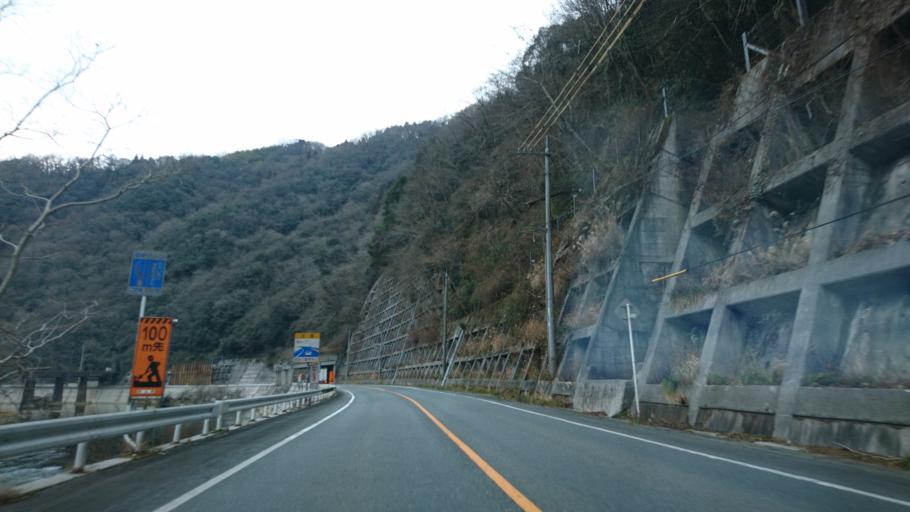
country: JP
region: Okayama
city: Niimi
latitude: 34.9117
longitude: 133.5321
